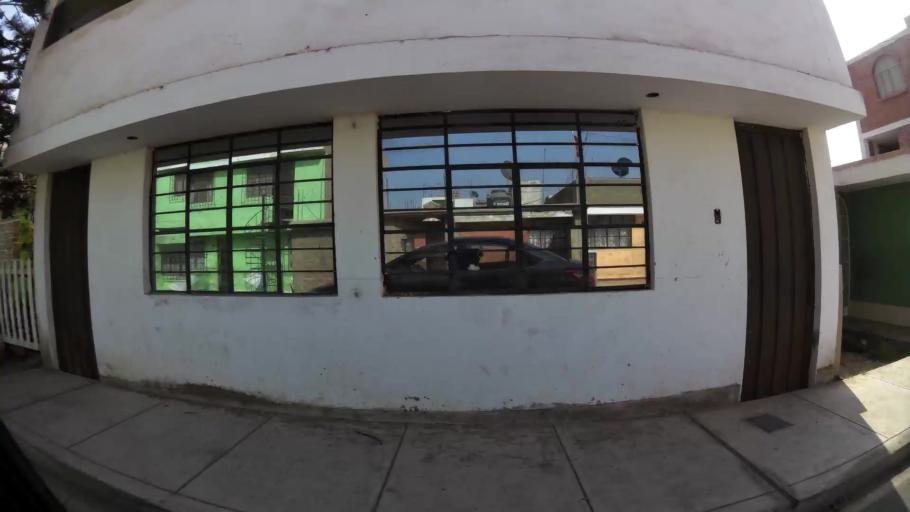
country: PE
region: Lima
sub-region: Lima
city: Santa Rosa
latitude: -11.7782
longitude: -77.1674
